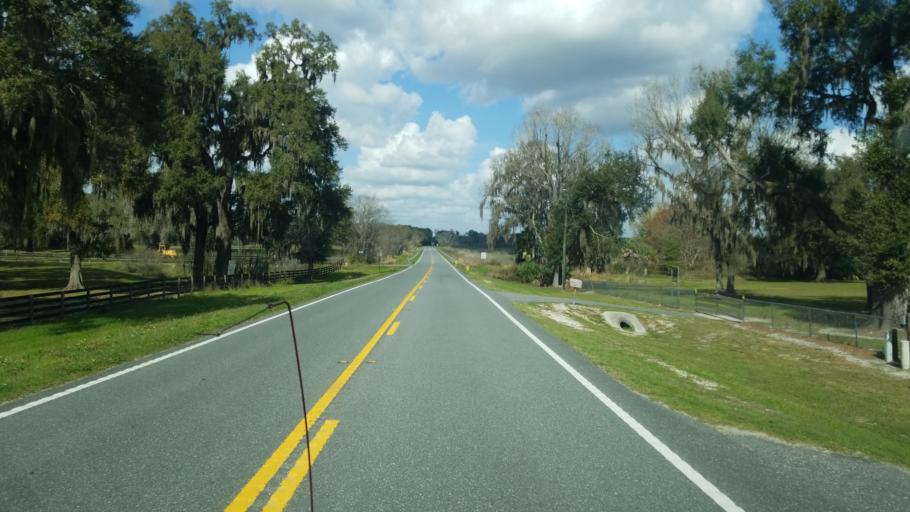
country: US
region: Florida
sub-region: Sumter County
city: Wildwood
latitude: 28.9224
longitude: -82.1199
